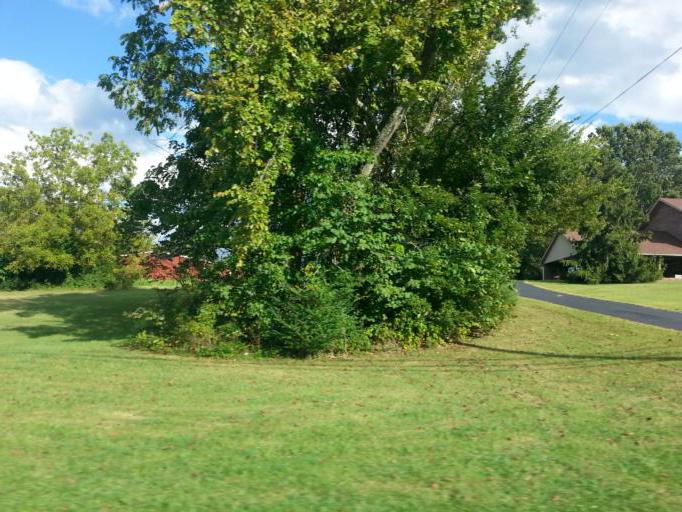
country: US
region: Tennessee
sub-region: Knox County
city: Mascot
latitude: 36.0907
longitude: -83.8188
